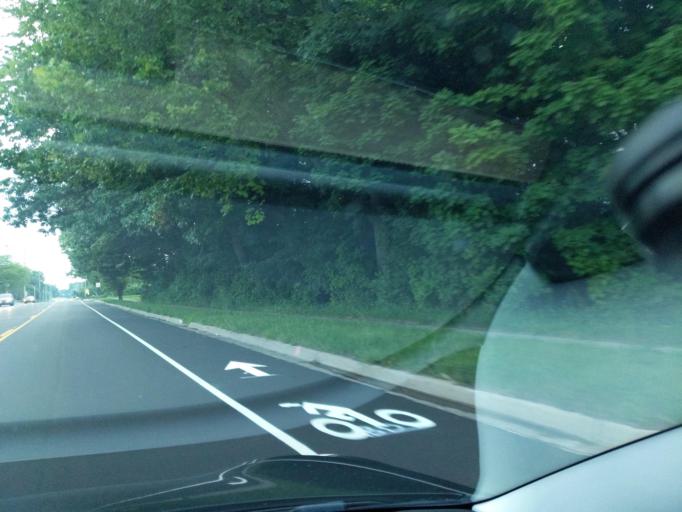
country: US
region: Michigan
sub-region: Eaton County
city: Waverly
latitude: 42.7338
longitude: -84.6248
